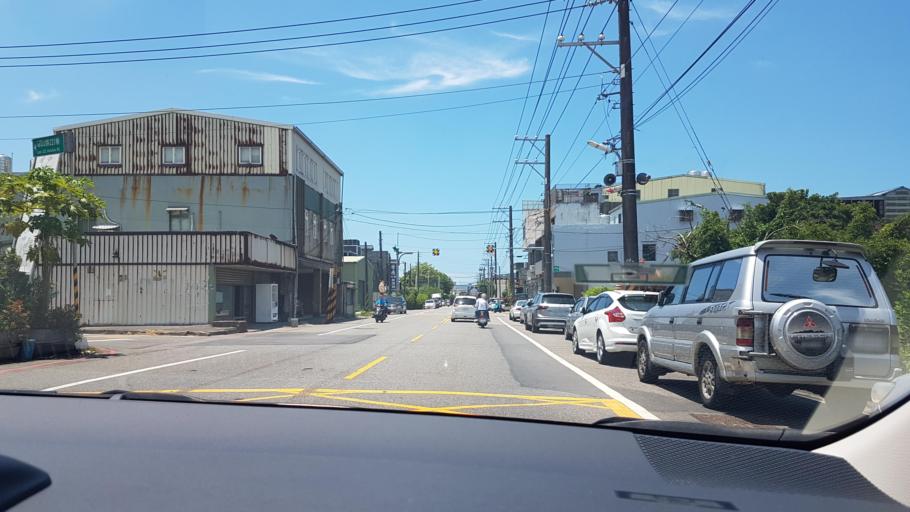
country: TW
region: Taiwan
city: Taoyuan City
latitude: 25.0872
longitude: 121.2813
